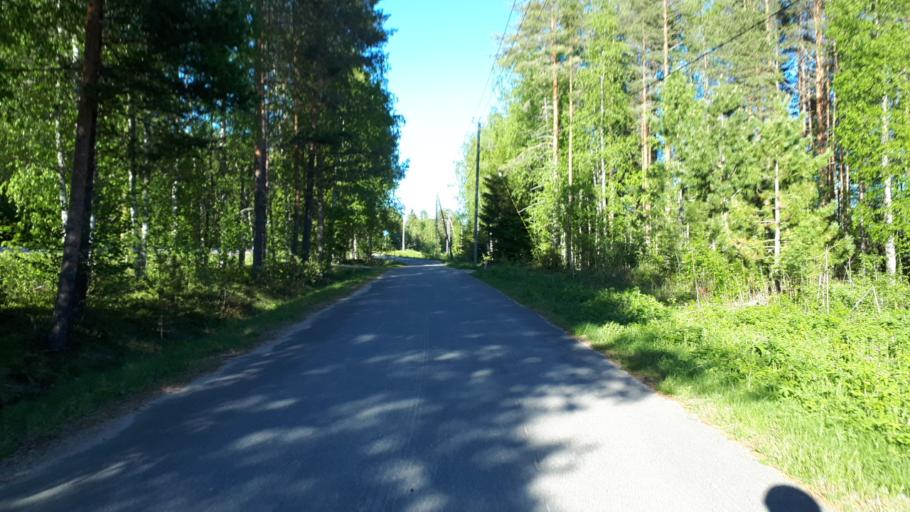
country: FI
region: Northern Ostrobothnia
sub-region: Oulunkaari
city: Ii
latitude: 65.3245
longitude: 25.4964
